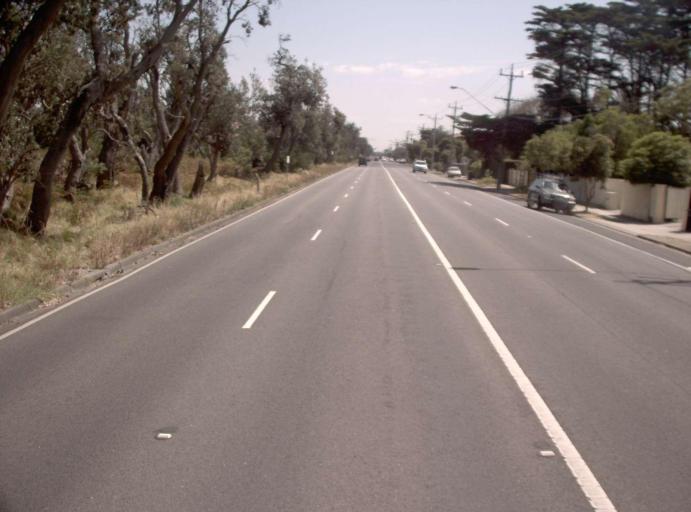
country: AU
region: Victoria
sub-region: Frankston
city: Seaford
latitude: -38.1148
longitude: 145.1256
